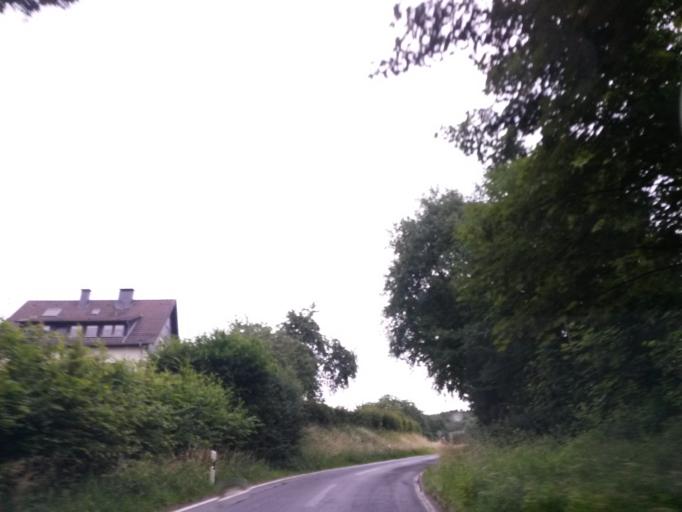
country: DE
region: North Rhine-Westphalia
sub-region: Regierungsbezirk Koln
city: Engelskirchen
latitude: 50.9558
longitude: 7.3616
